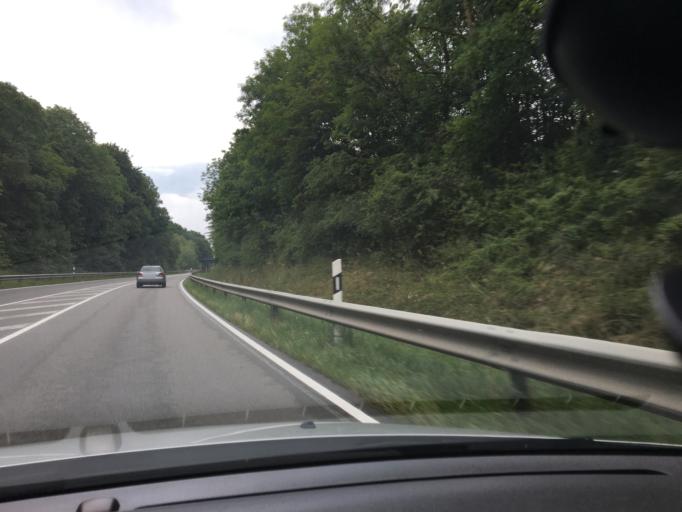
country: DE
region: Bavaria
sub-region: Upper Bavaria
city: Mettenheim
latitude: 48.2462
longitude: 12.4790
